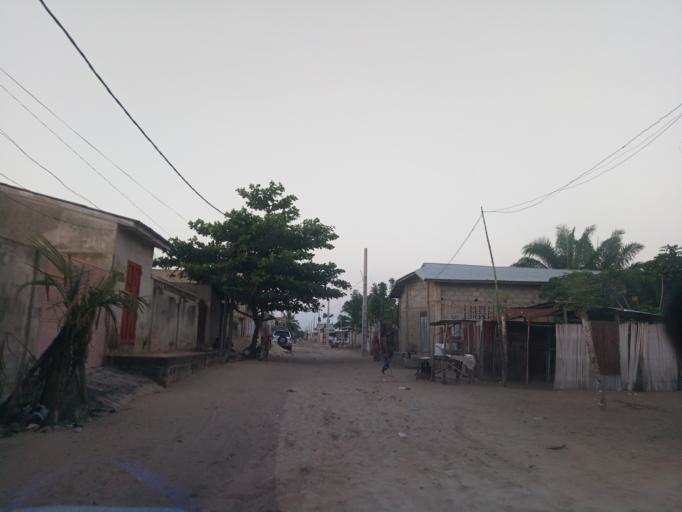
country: BJ
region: Atlantique
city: Hevie
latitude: 6.3909
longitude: 2.2880
